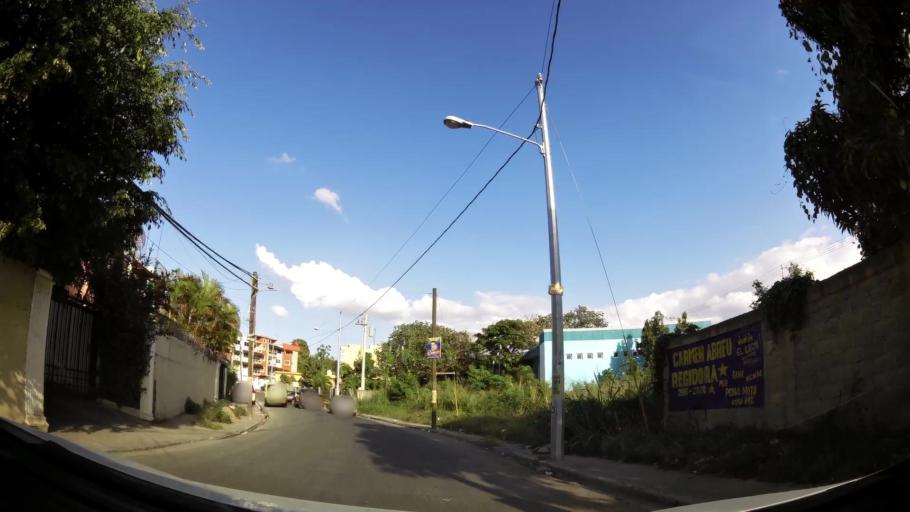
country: DO
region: Nacional
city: Ensanche Luperon
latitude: 18.5477
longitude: -69.9056
